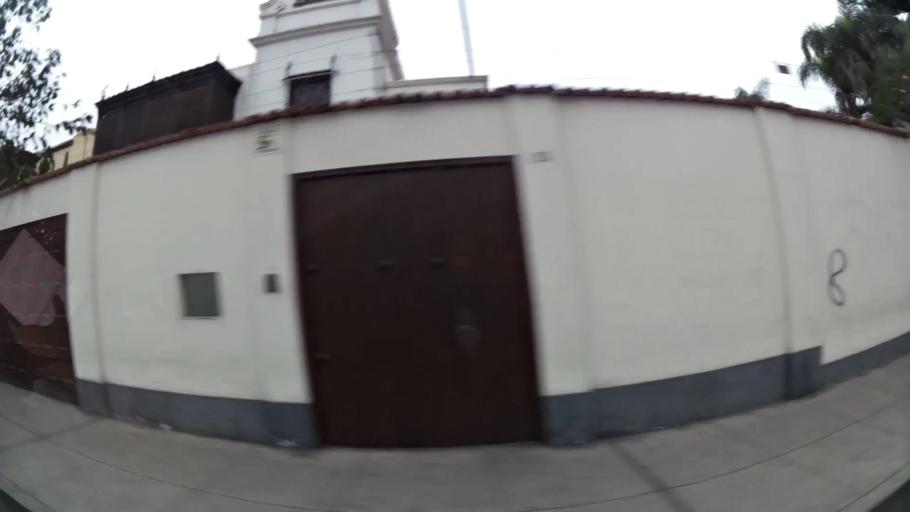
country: PE
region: Lima
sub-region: Lima
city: Surco
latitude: -12.1551
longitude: -77.0223
